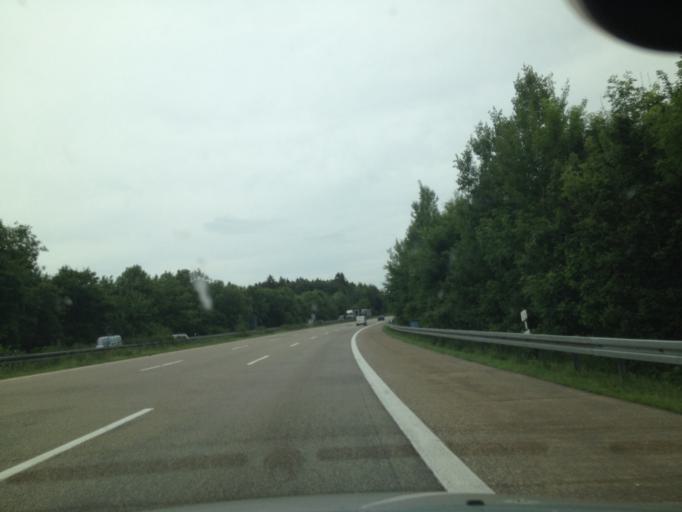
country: DE
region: North Rhine-Westphalia
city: Meinerzhagen
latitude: 51.0836
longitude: 7.6907
